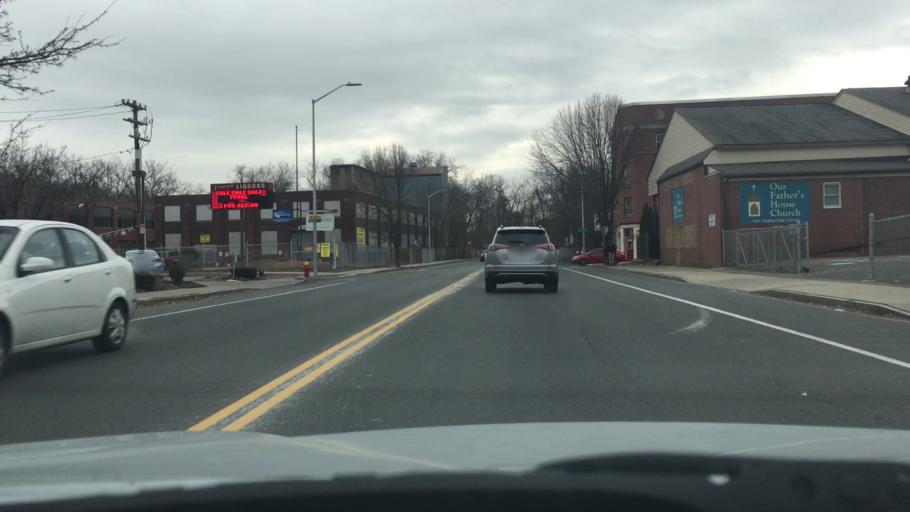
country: US
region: Massachusetts
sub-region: Hampden County
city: North Chicopee
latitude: 42.1907
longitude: -72.6024
